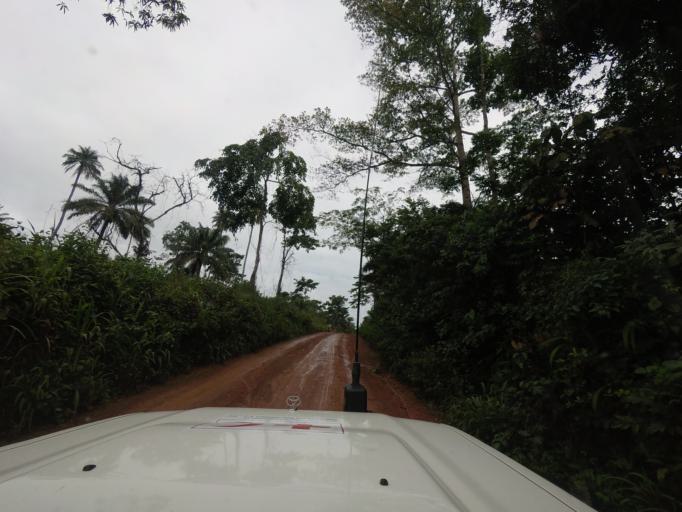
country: GN
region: Nzerekore
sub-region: Nzerekore Prefecture
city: Nzerekore
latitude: 7.7268
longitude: -8.8614
